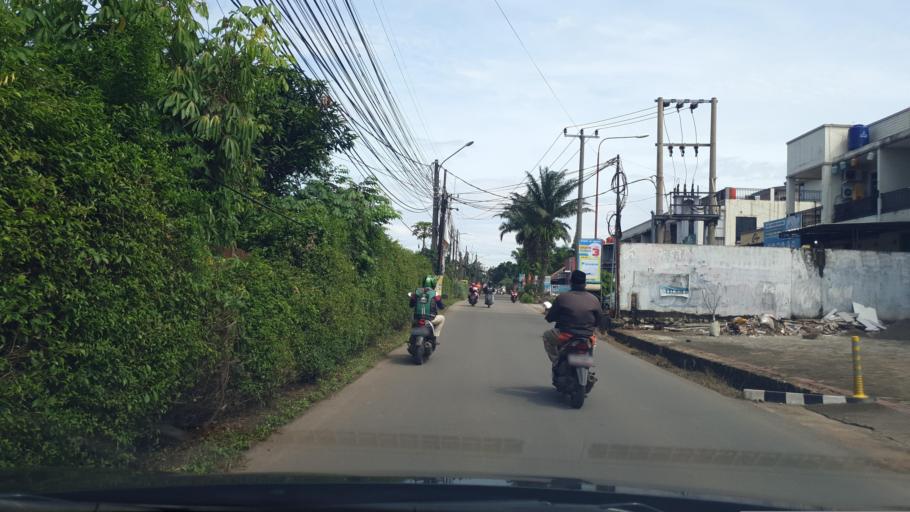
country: ID
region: West Java
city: Sawangan
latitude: -6.4090
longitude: 106.7702
